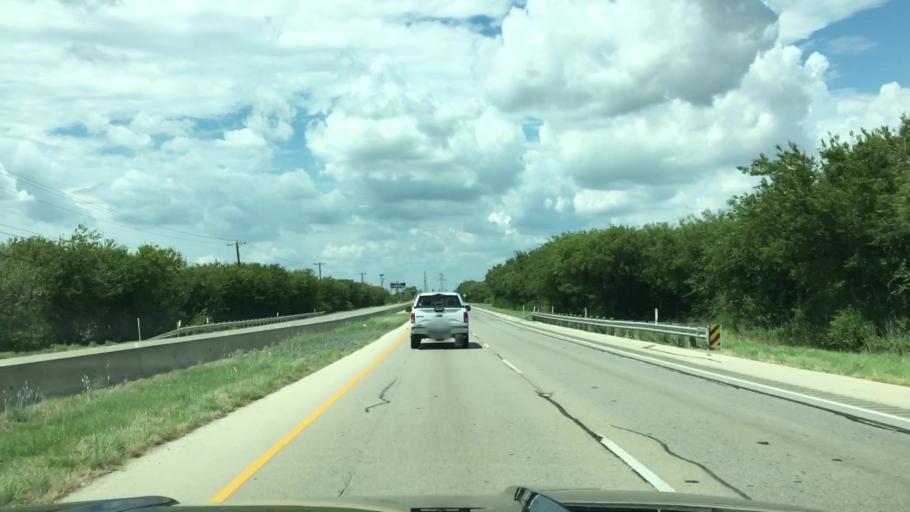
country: US
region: Texas
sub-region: Tarrant County
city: Saginaw
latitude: 32.8961
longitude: -97.3949
